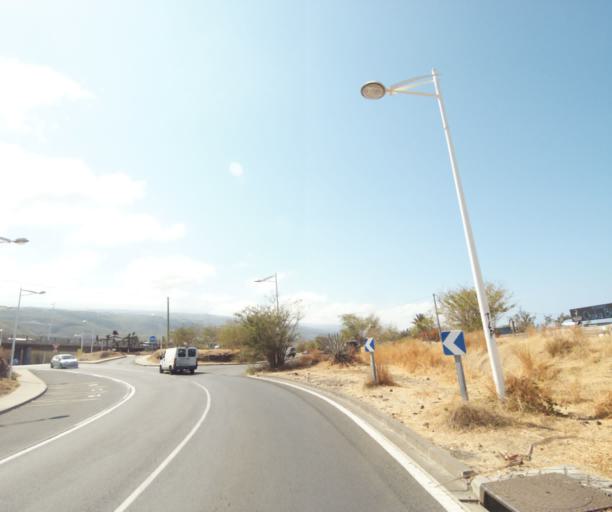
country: RE
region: Reunion
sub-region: Reunion
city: Trois-Bassins
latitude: -21.1029
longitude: 55.2469
